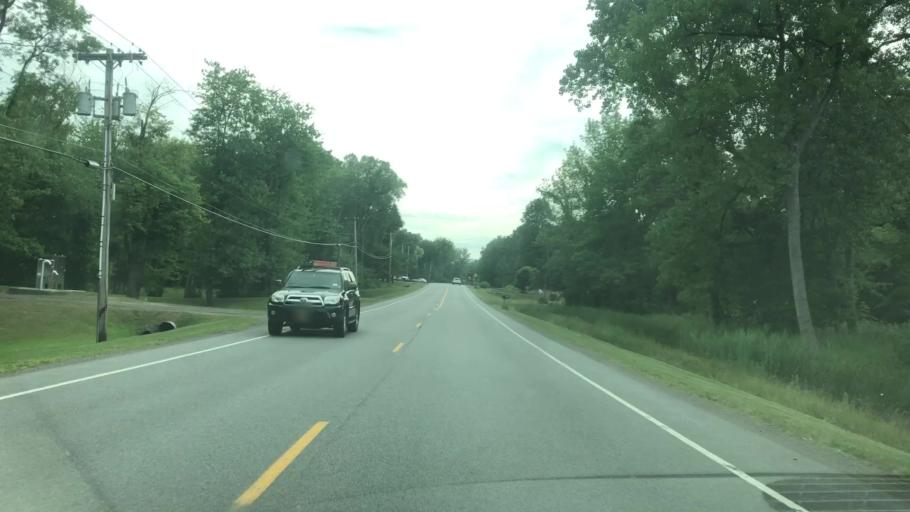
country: US
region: New York
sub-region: Monroe County
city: Fairport
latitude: 43.1331
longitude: -77.3679
